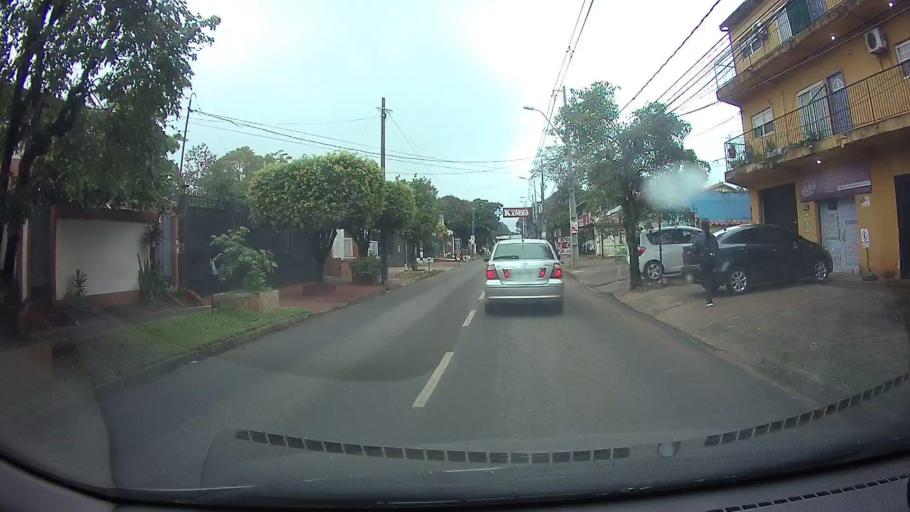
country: PY
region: Central
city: Fernando de la Mora
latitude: -25.3353
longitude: -57.5609
